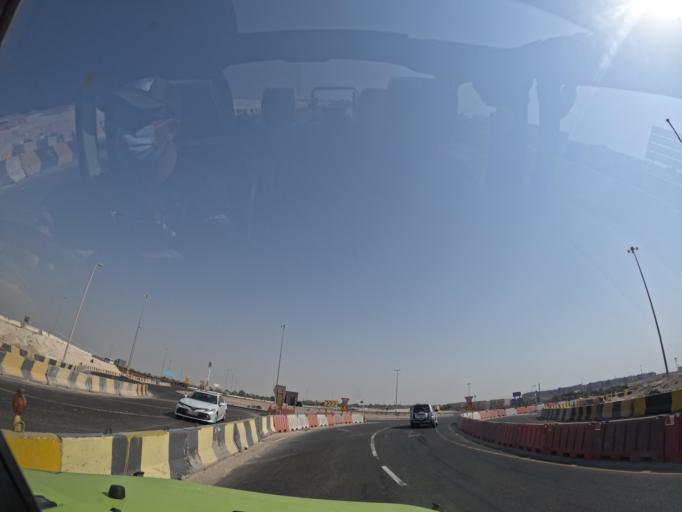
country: AE
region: Abu Dhabi
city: Abu Dhabi
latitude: 24.4647
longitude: 54.6737
